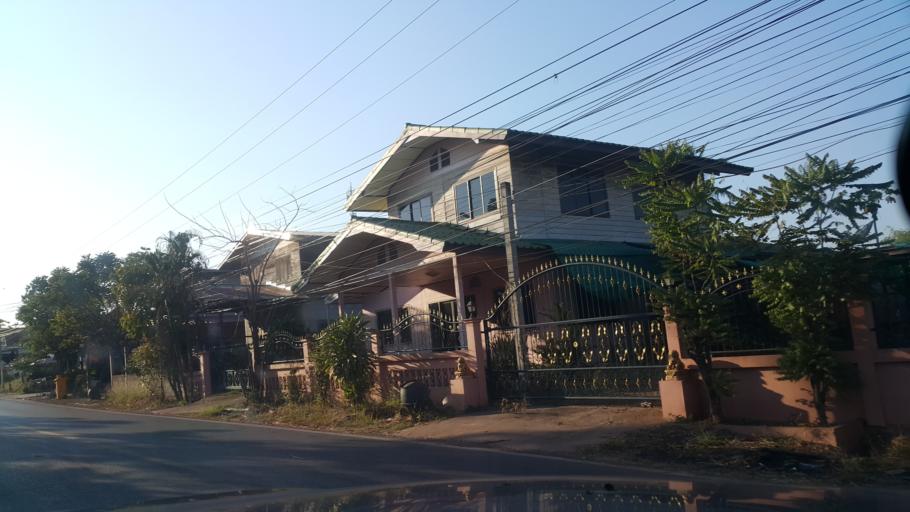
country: TH
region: Changwat Udon Thani
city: Ban Na Muang
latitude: 17.2669
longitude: 103.0041
